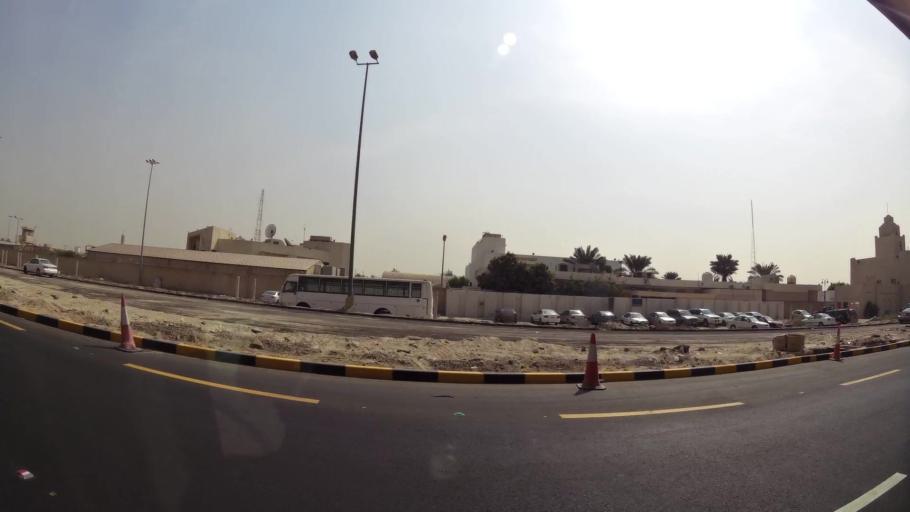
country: KW
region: Al Asimah
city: Ar Rabiyah
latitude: 29.3250
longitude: 47.9163
